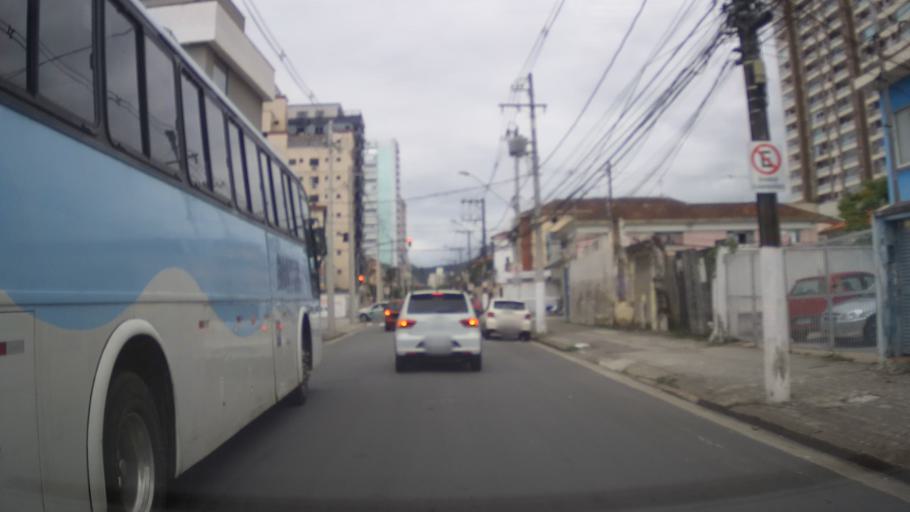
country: BR
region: Sao Paulo
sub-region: Santos
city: Santos
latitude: -23.9568
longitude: -46.3270
